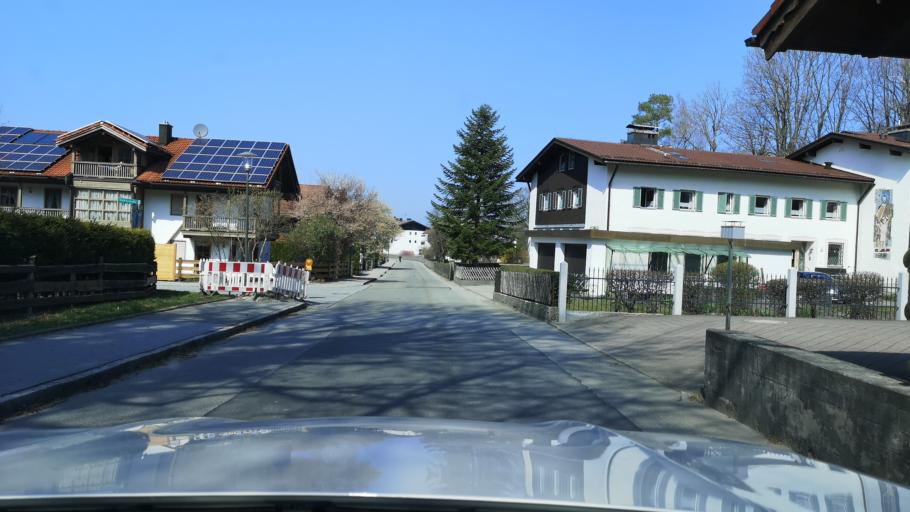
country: DE
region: Bavaria
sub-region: Upper Bavaria
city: Bad Feilnbach
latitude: 47.7704
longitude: 12.0130
